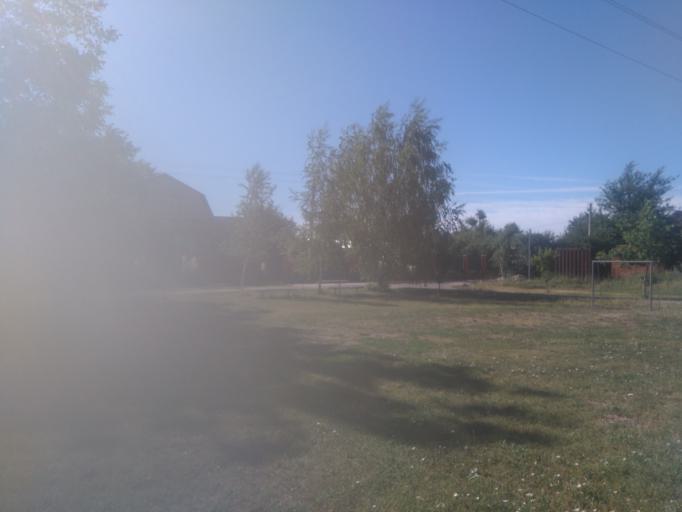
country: RU
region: Krasnodarskiy
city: Fastovetskaya
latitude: 45.9073
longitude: 40.1507
